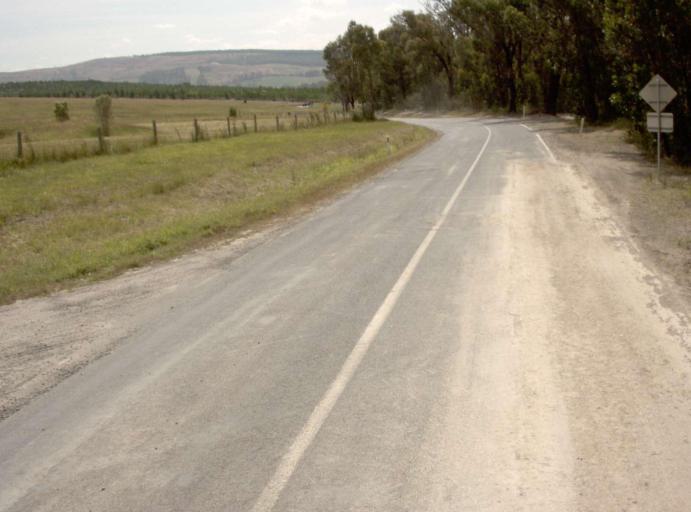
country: AU
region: Victoria
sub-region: Latrobe
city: Traralgon
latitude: -38.3111
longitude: 146.5628
